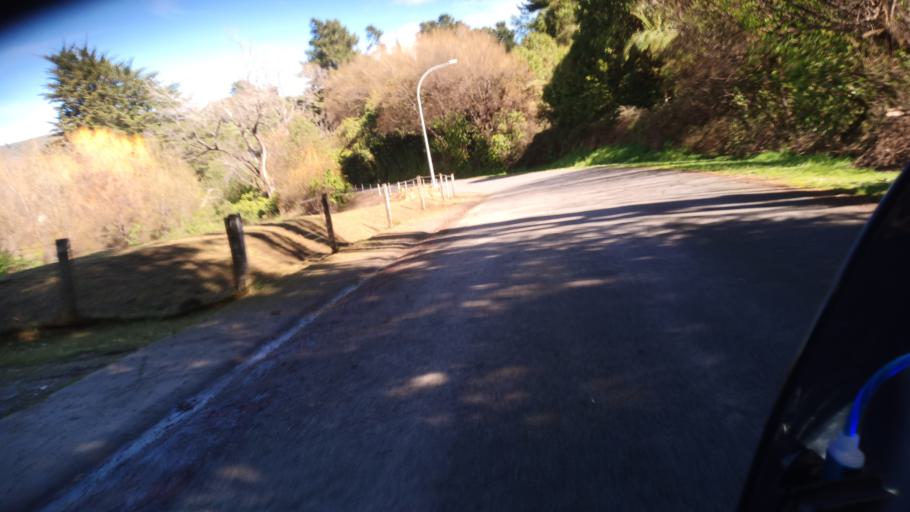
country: NZ
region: Hawke's Bay
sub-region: Wairoa District
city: Wairoa
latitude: -38.8157
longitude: 177.1461
